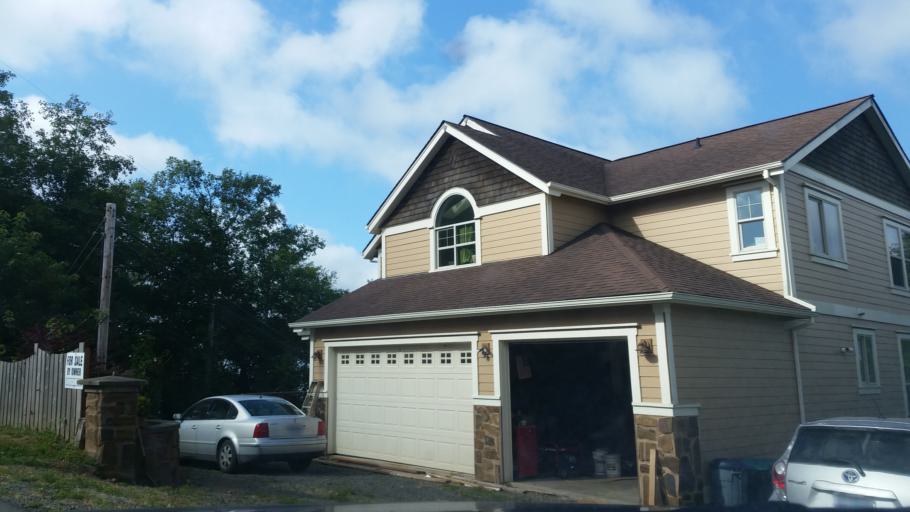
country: US
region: Oregon
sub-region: Clatsop County
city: Astoria
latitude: 46.1830
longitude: -123.8503
